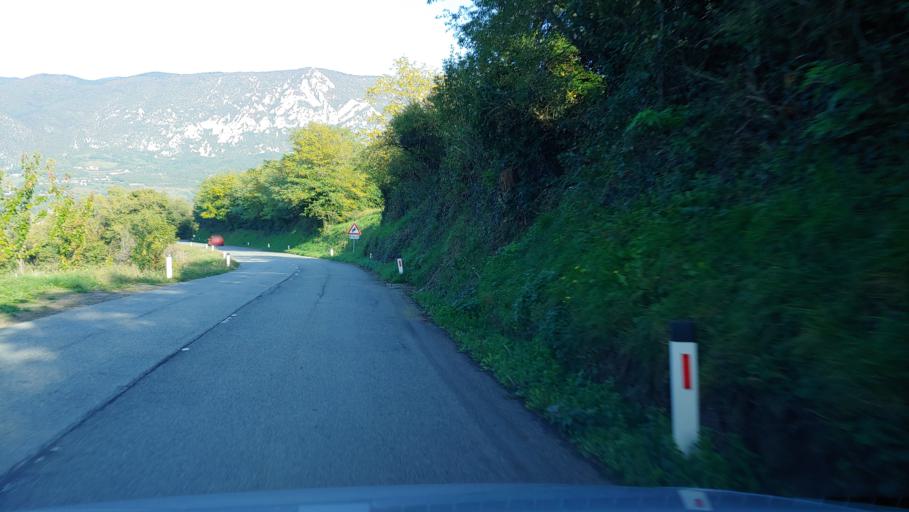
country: SI
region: Vipava
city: Vipava
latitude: 45.8169
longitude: 13.9343
